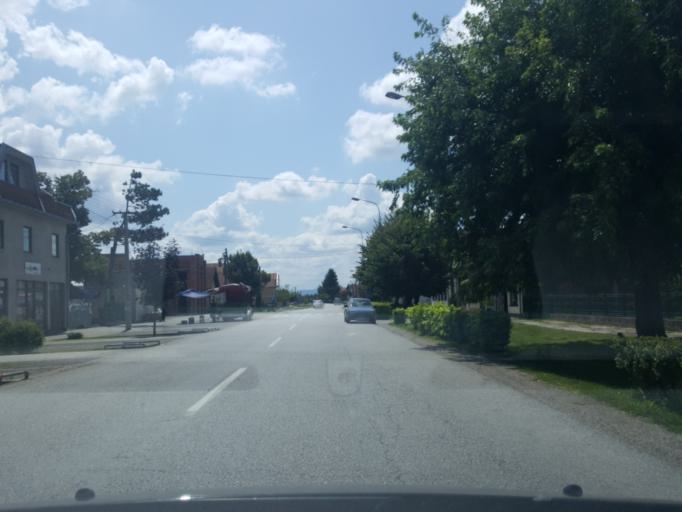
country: RS
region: Central Serbia
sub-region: Macvanski Okrug
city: Bogatic
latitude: 44.8316
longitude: 19.4790
